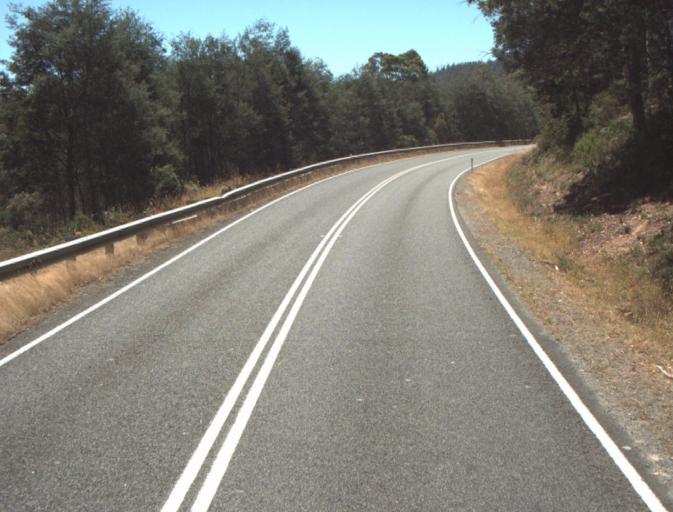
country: AU
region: Tasmania
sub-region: Dorset
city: Scottsdale
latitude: -41.3004
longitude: 147.3824
